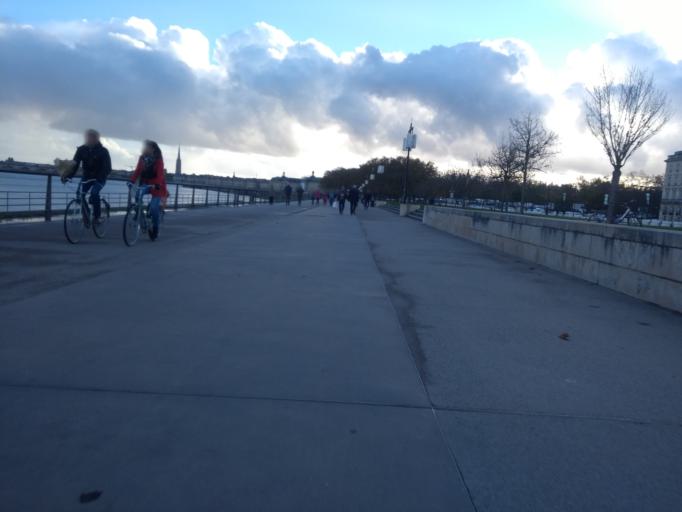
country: FR
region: Aquitaine
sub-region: Departement de la Gironde
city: Bordeaux
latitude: 44.8489
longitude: -0.5698
